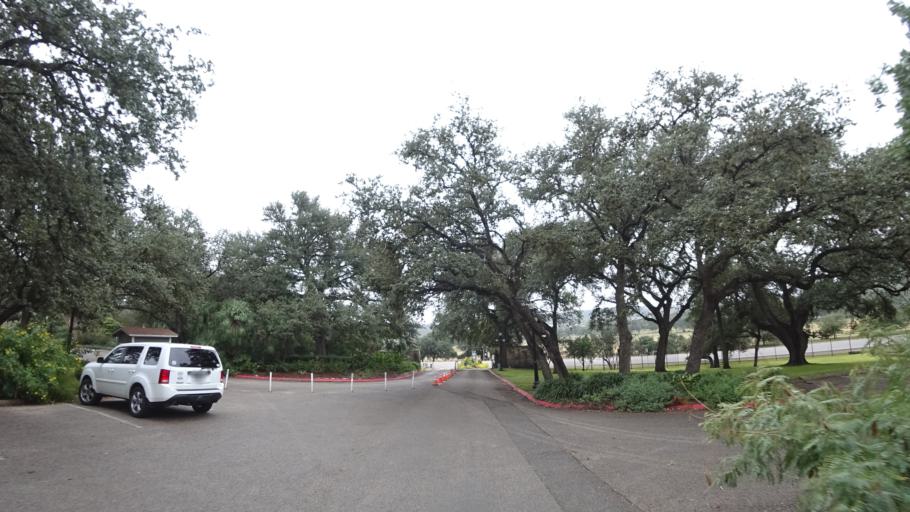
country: US
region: Texas
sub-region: Travis County
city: Rollingwood
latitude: 30.2689
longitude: -97.7725
